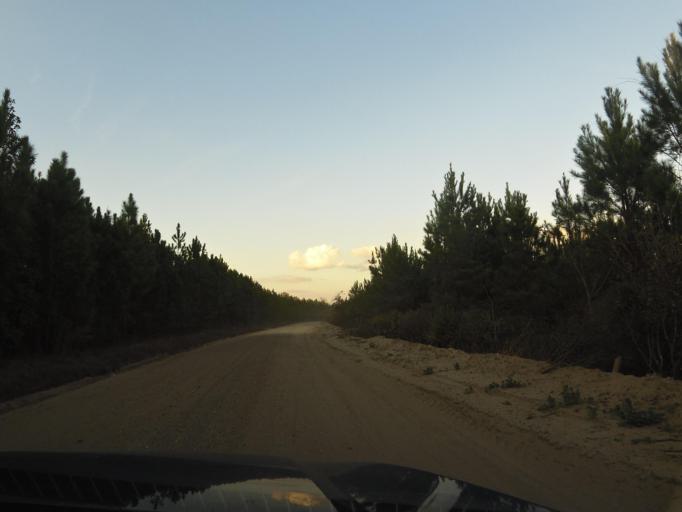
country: US
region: Florida
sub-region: Clay County
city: Keystone Heights
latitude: 29.8287
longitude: -81.8203
